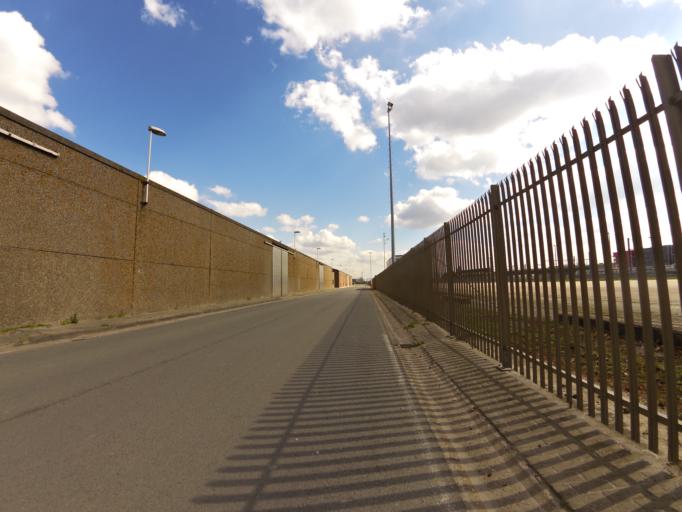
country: BE
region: Flanders
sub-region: Provincie West-Vlaanderen
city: Ostend
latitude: 51.2222
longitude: 2.9342
